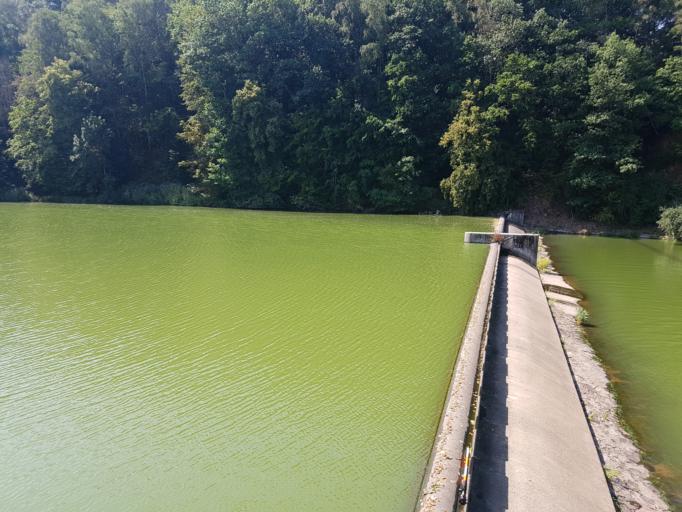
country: DE
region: Saxony
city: Kriebstein
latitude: 51.0497
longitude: 13.0147
